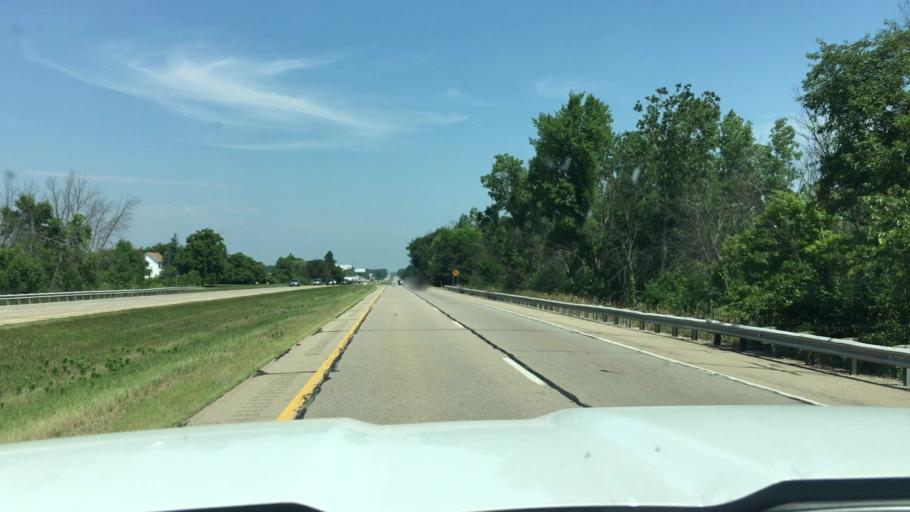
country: US
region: Michigan
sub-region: Clinton County
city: Saint Johns
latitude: 43.0831
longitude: -84.5636
